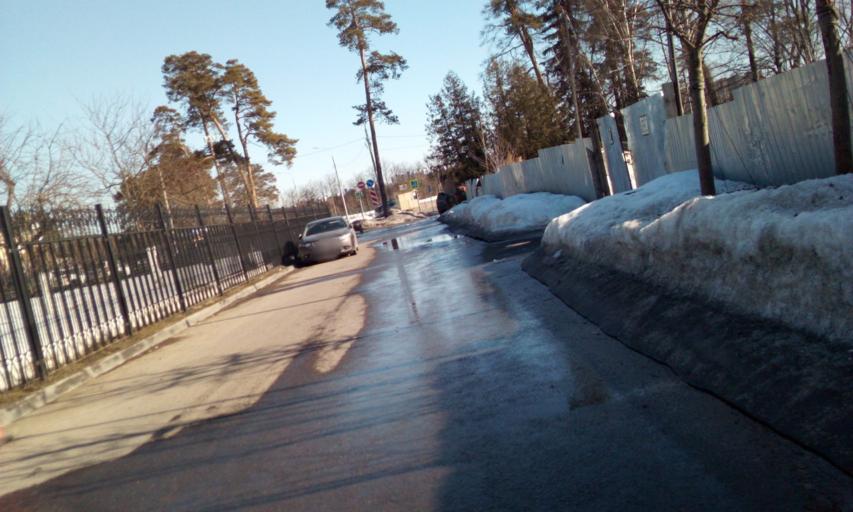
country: RU
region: Moscow
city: Novo-Peredelkino
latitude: 55.6570
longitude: 37.3453
